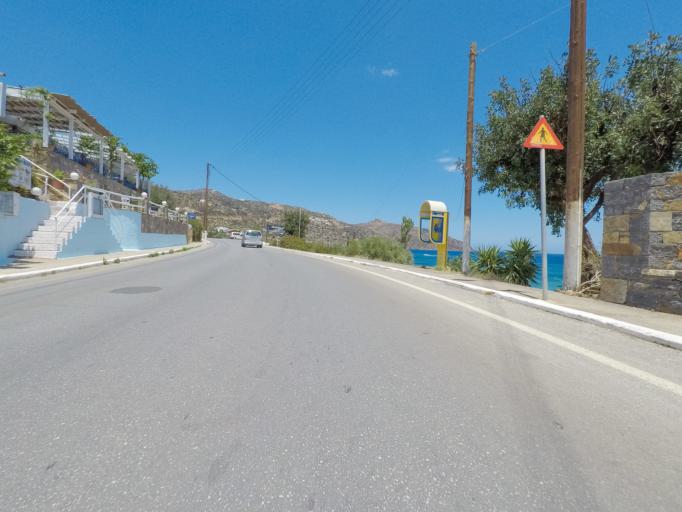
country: GR
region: Crete
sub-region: Nomos Lasithiou
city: Agios Nikolaos
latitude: 35.2126
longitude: 25.7117
